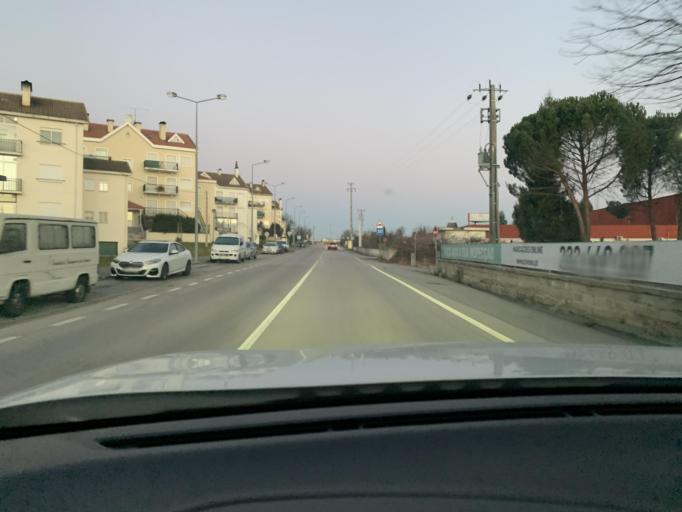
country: PT
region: Viseu
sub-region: Viseu
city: Viseu
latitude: 40.6323
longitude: -7.9048
